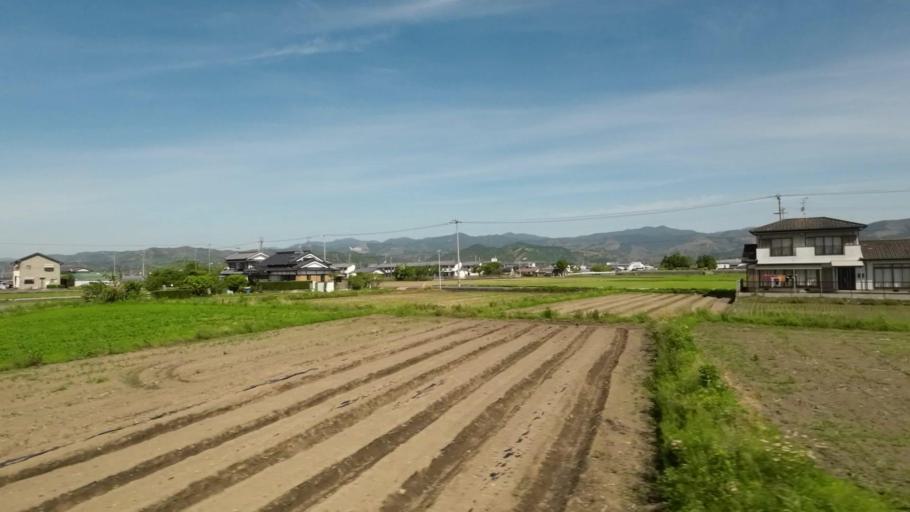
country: JP
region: Kochi
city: Kochi-shi
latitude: 33.5870
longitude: 133.6568
